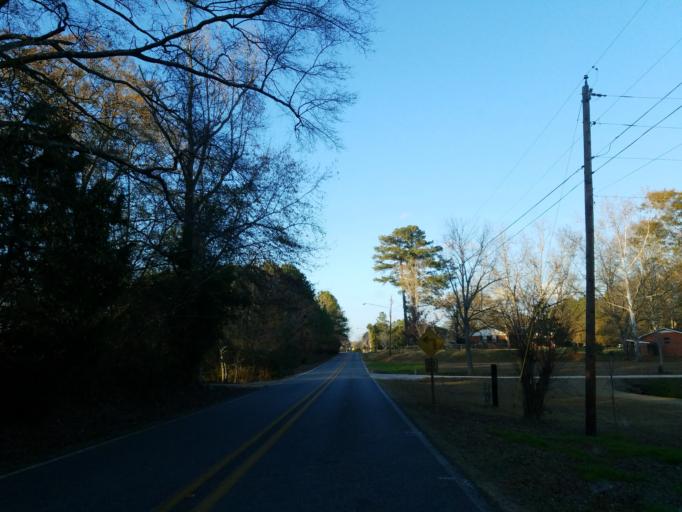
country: US
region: Mississippi
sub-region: Clarke County
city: Stonewall
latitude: 32.1784
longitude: -88.8284
